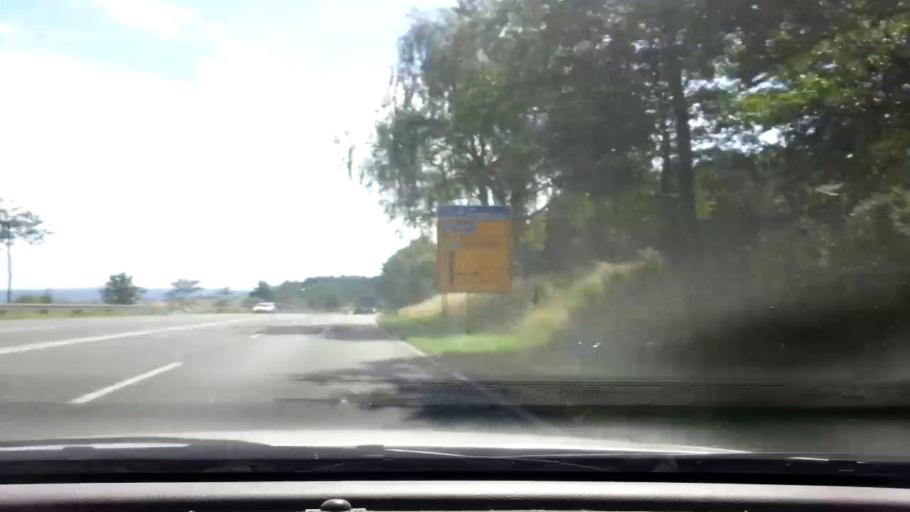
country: DE
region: Bavaria
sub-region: Upper Palatinate
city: Waldershof
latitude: 50.0120
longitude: 12.0546
